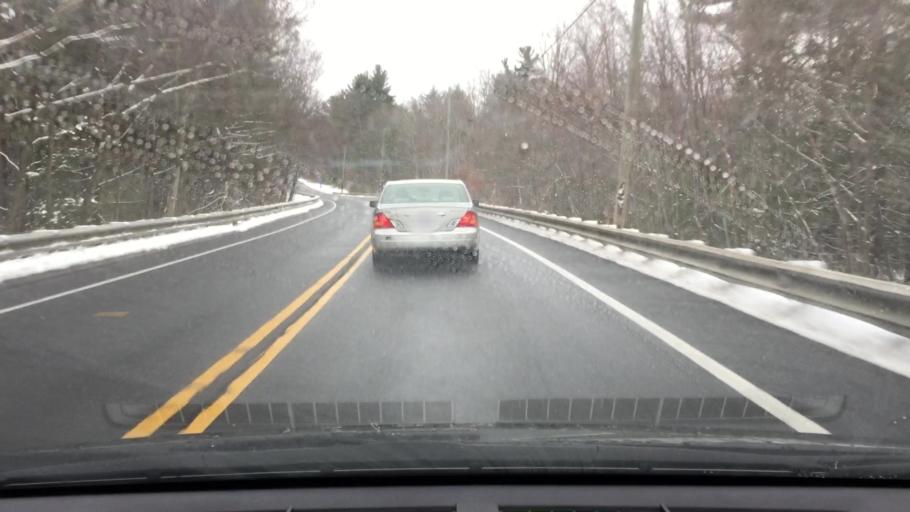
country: US
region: Massachusetts
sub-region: Hampshire County
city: Pelham
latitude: 42.3563
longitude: -72.4022
